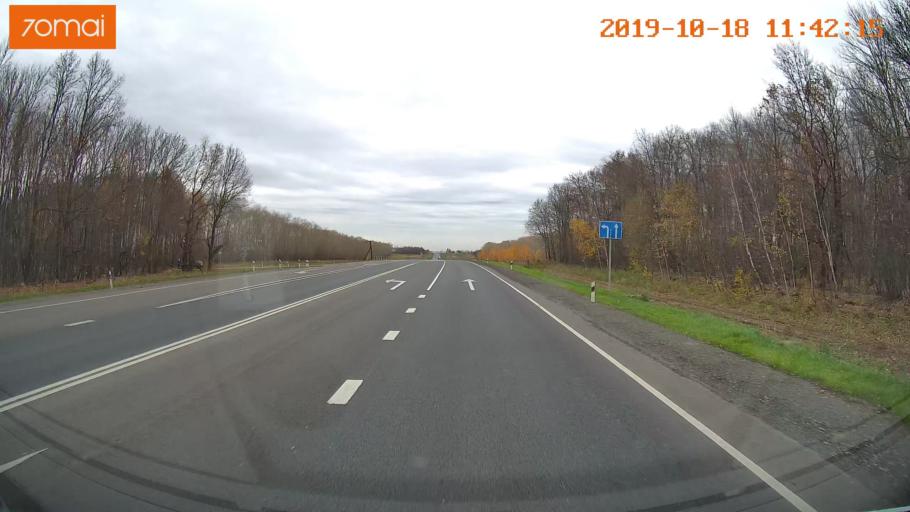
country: RU
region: Rjazan
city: Oktyabr'skiy
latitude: 54.1864
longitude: 38.9241
